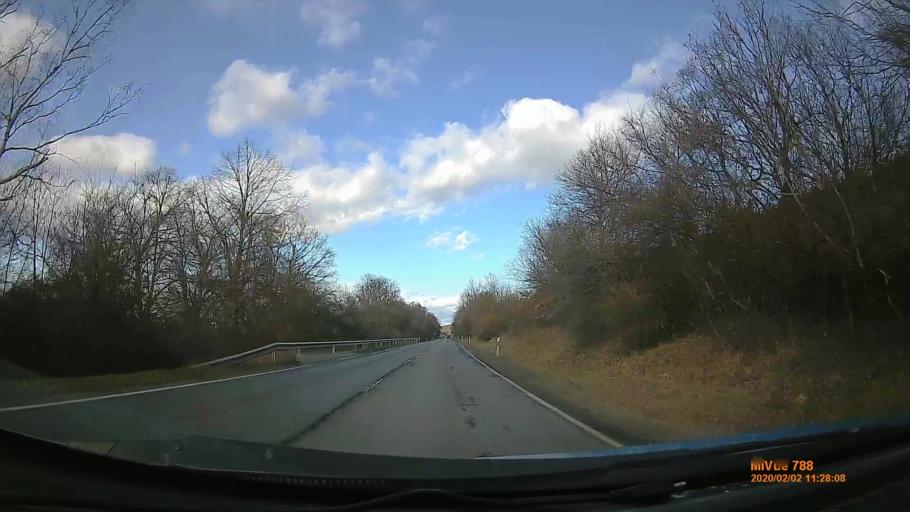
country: AT
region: Burgenland
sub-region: Eisenstadt-Umgebung
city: Klingenbach
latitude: 47.7245
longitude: 16.5614
